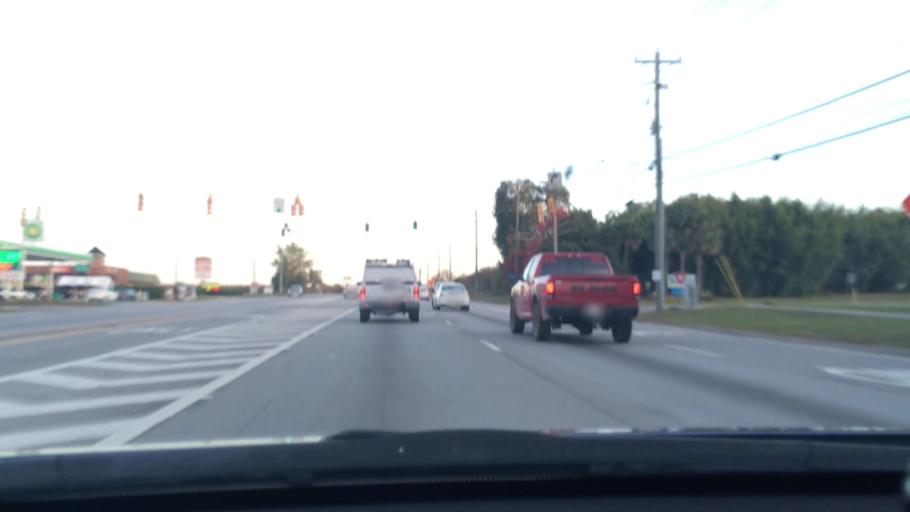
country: US
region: South Carolina
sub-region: Richland County
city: Hopkins
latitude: 33.9533
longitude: -80.9223
